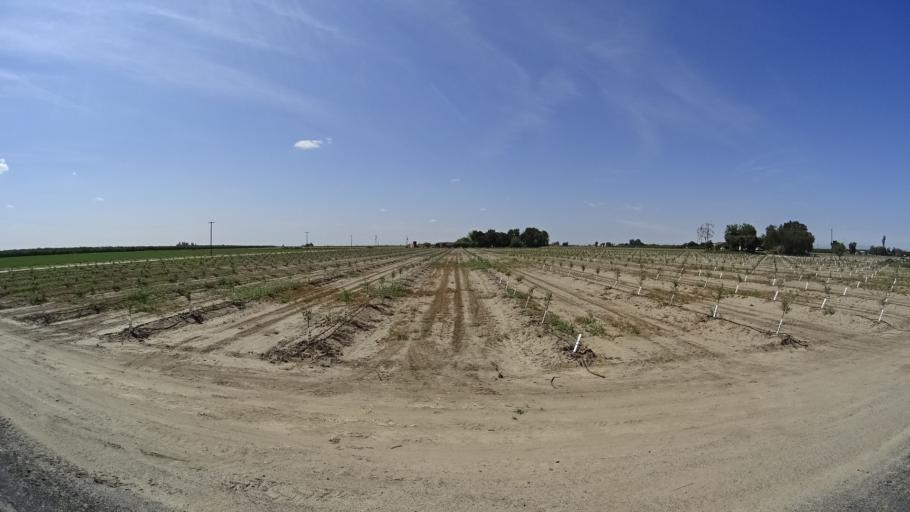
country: US
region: California
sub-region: Kings County
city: Lemoore
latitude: 36.2695
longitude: -119.7402
